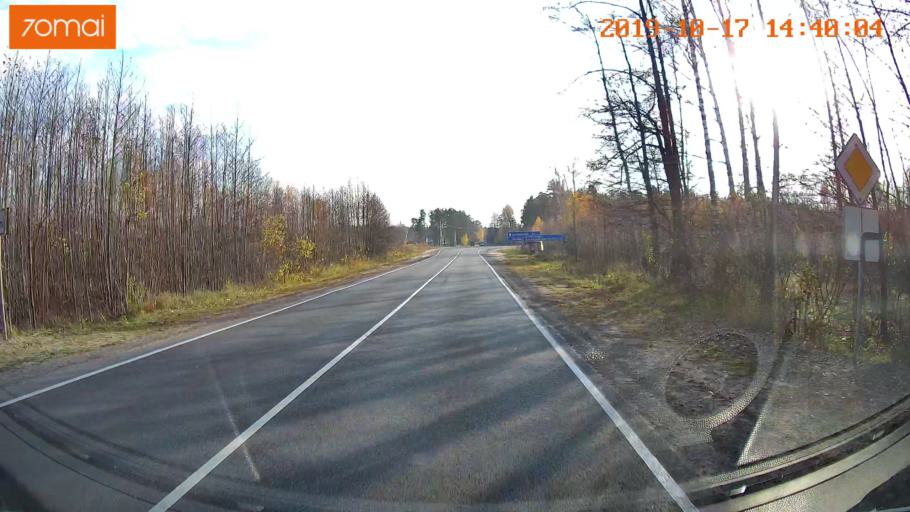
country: RU
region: Rjazan
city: Solotcha
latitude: 54.8571
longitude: 39.9615
